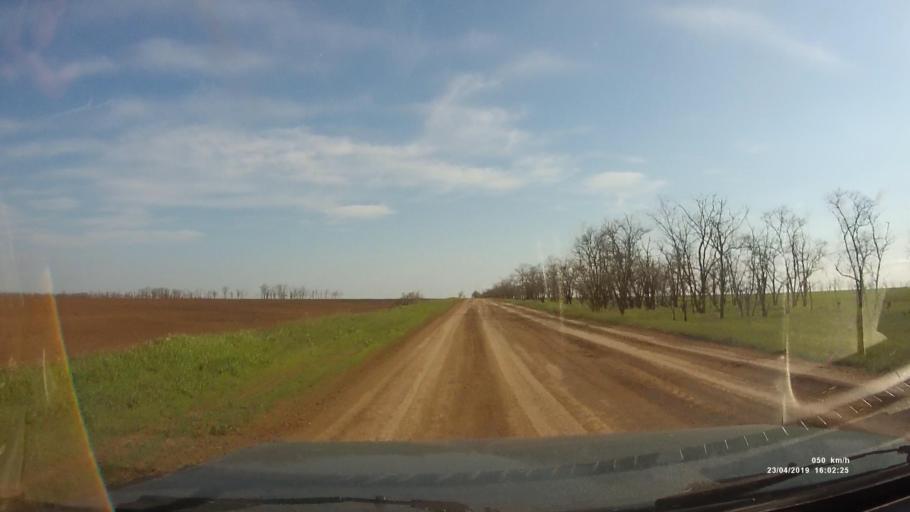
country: RU
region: Rostov
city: Remontnoye
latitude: 46.4945
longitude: 43.1070
